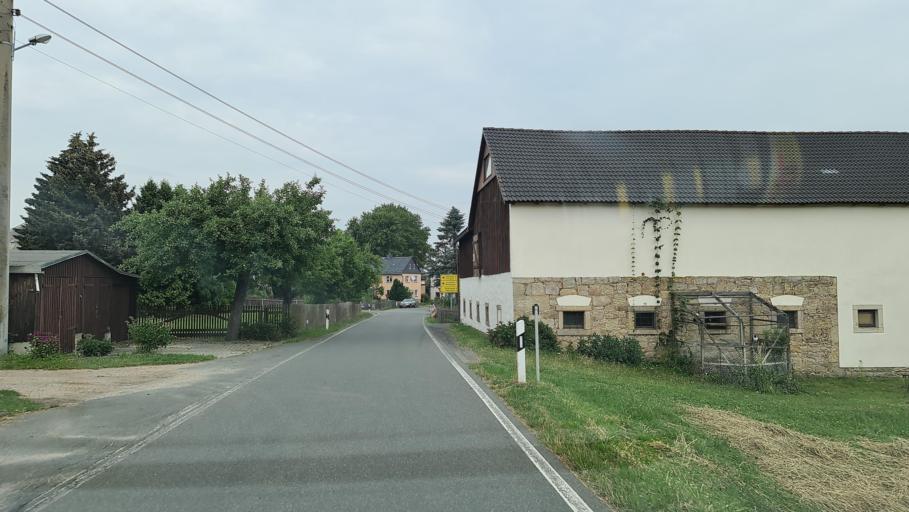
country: DE
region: Saxony
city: Hirschfeld
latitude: 50.5821
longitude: 12.4478
